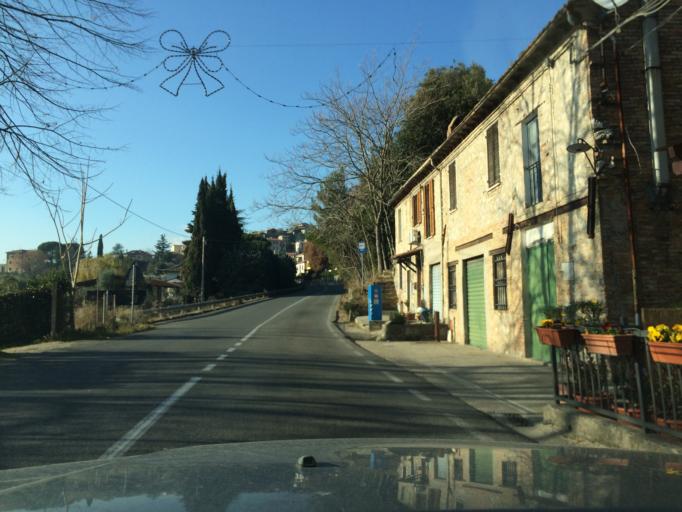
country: IT
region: Umbria
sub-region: Provincia di Terni
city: Fornole
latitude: 42.5423
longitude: 12.4617
